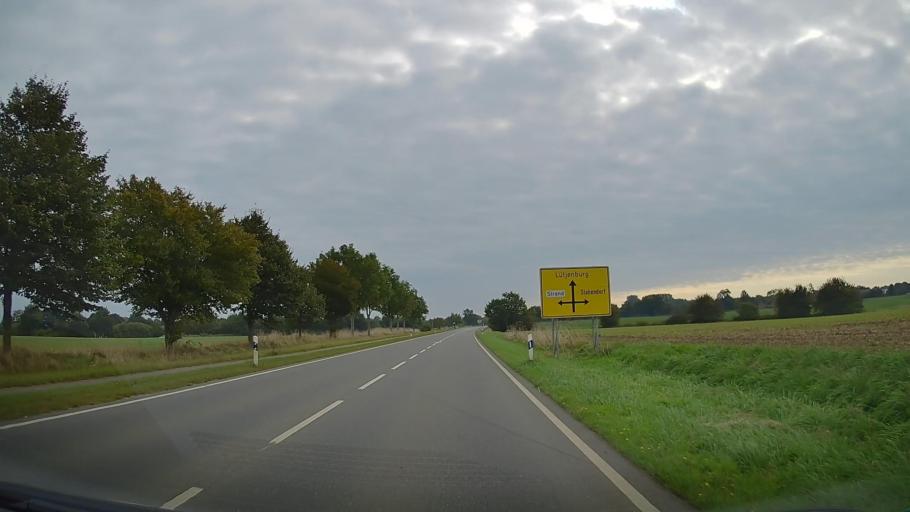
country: DE
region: Schleswig-Holstein
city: Stakendorf
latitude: 54.3967
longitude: 10.4175
